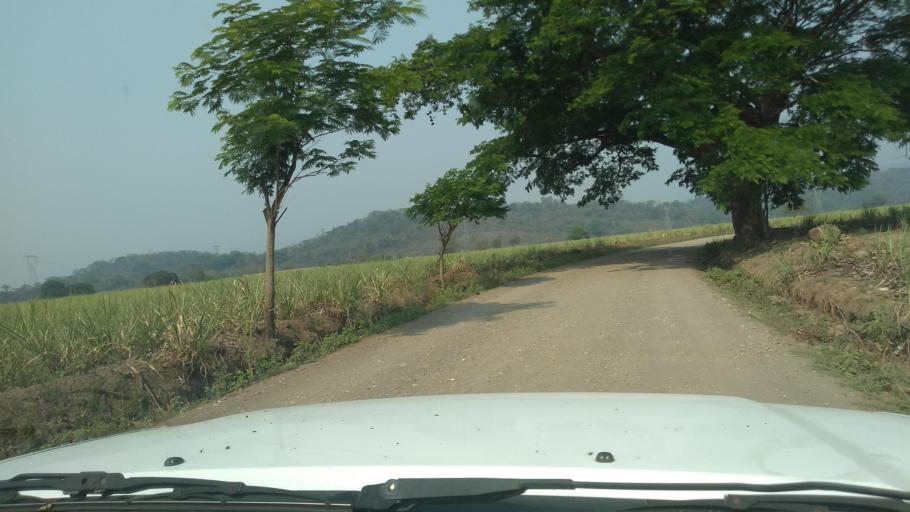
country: MX
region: Oaxaca
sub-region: Cosolapa
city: Cosolapa
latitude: 18.6185
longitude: -96.6288
